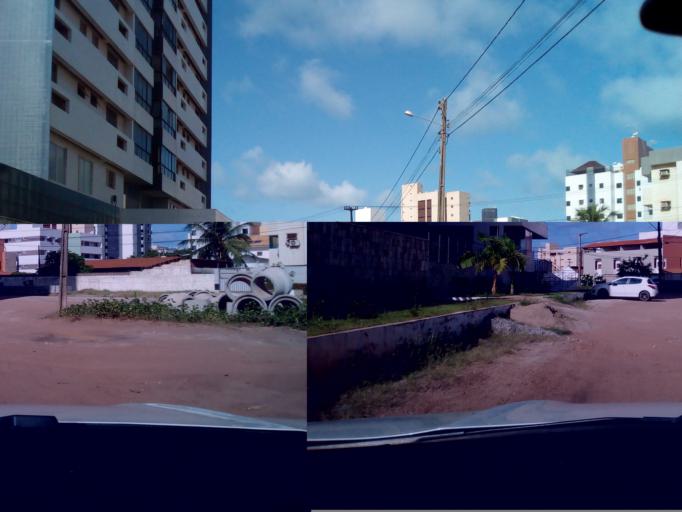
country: BR
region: Paraiba
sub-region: Cabedelo
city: Cabedelo
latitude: -7.0368
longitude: -34.8419
